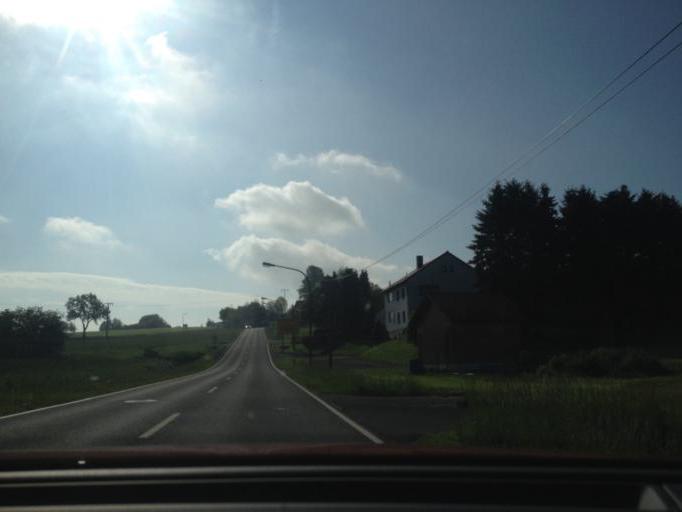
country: DE
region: Bavaria
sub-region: Upper Franconia
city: Prebitz
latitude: 49.7759
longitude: 11.6569
